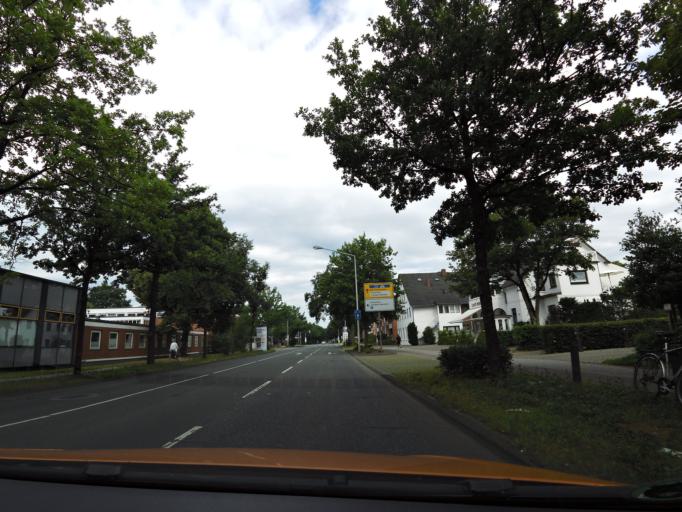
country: DE
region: Lower Saxony
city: Oldenburg
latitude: 53.1475
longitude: 8.1844
